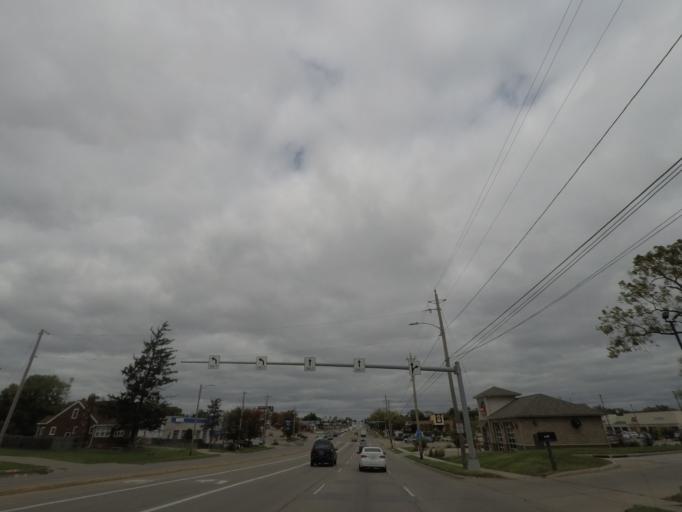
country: US
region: Iowa
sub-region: Polk County
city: Des Moines
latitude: 41.5519
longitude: -93.5967
